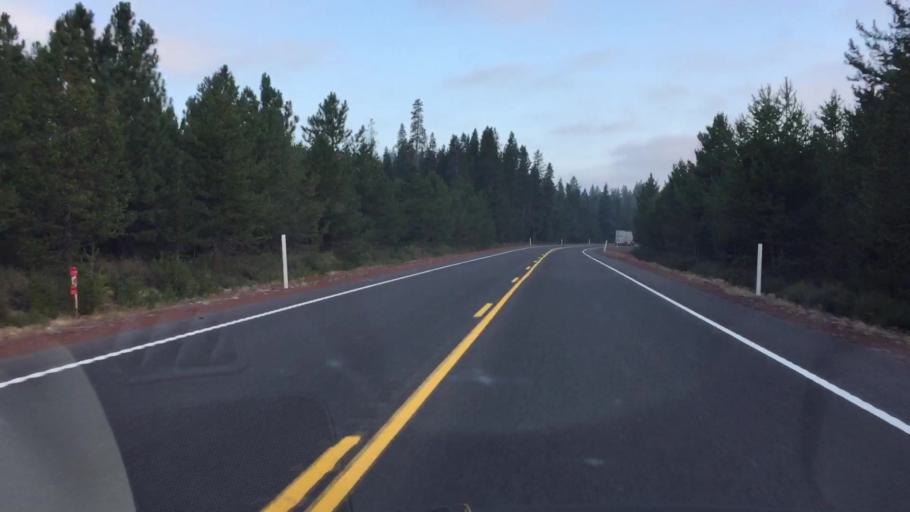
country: US
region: Oregon
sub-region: Deschutes County
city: La Pine
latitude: 43.3080
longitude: -121.7671
